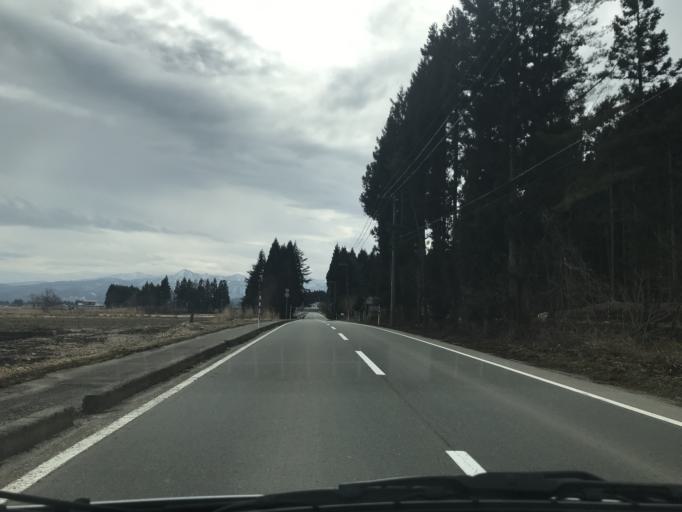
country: JP
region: Iwate
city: Hanamaki
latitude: 39.3533
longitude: 140.9865
